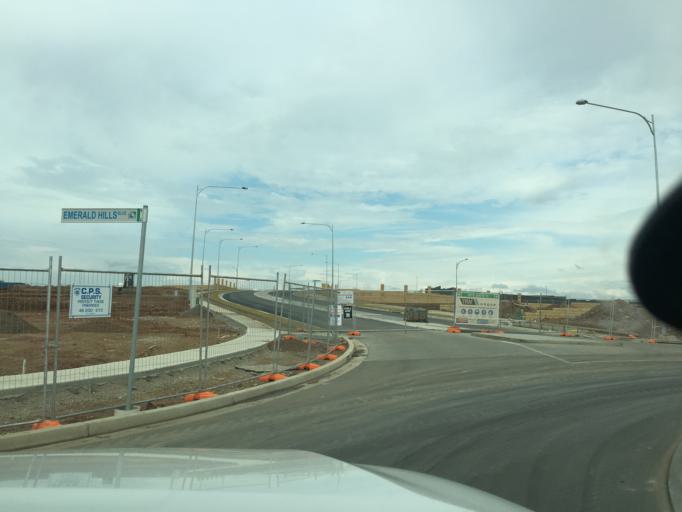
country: AU
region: New South Wales
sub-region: Campbelltown Municipality
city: Denham Court
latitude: -33.9872
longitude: 150.7975
